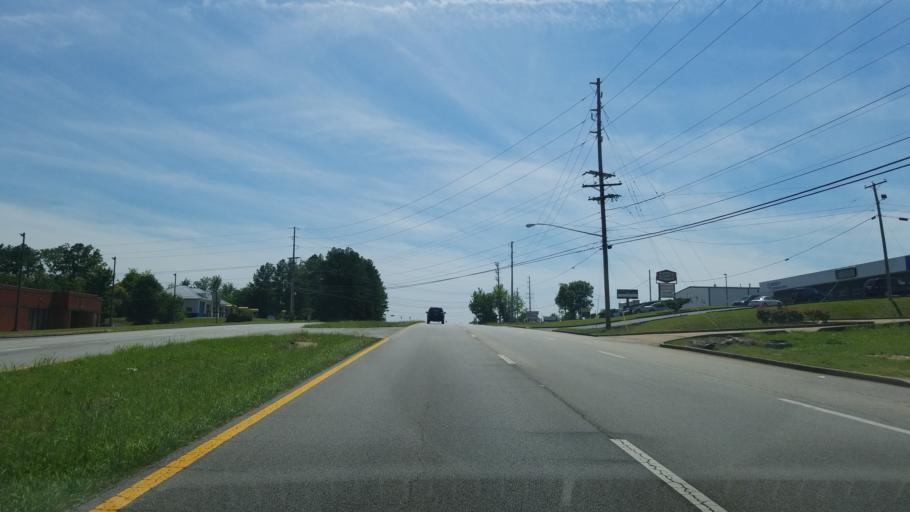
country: US
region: Tennessee
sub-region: Hamilton County
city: East Brainerd
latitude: 35.0355
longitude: -85.1774
